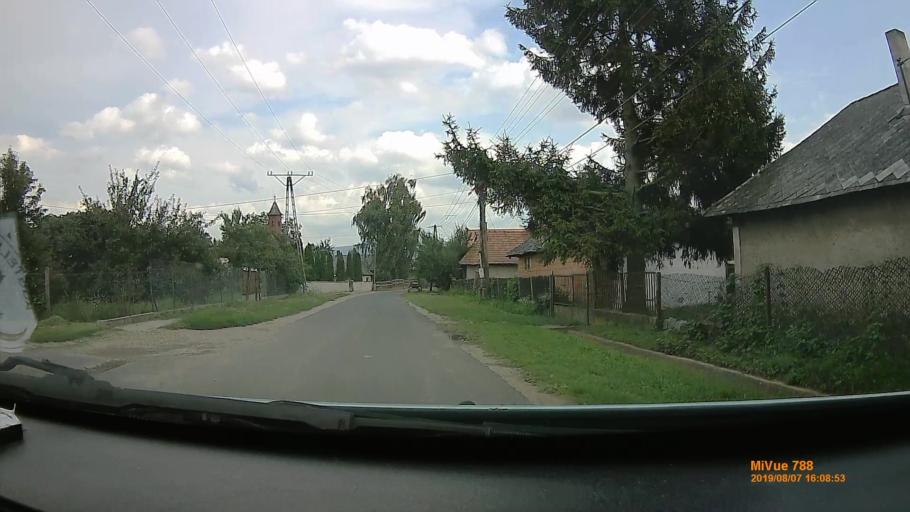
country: HU
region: Borsod-Abauj-Zemplen
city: Gonc
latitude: 48.5011
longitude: 21.2275
